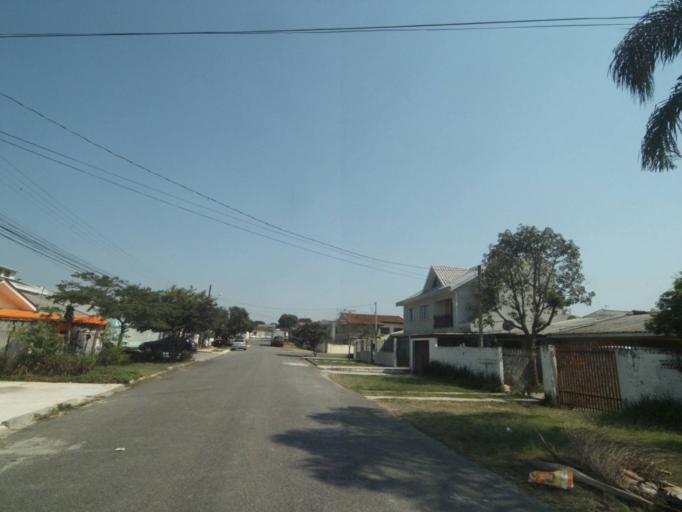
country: BR
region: Parana
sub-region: Sao Jose Dos Pinhais
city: Sao Jose dos Pinhais
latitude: -25.5210
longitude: -49.2706
